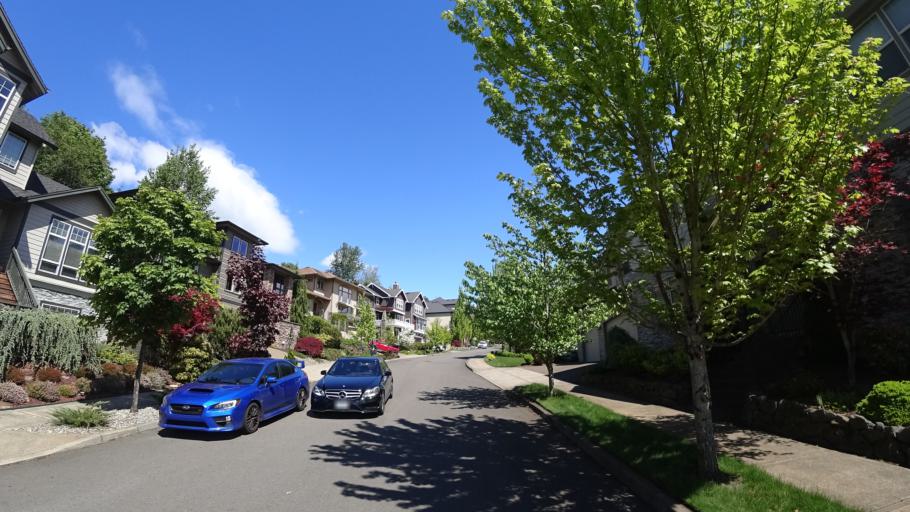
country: US
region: Oregon
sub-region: Washington County
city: West Haven
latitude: 45.5509
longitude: -122.7807
